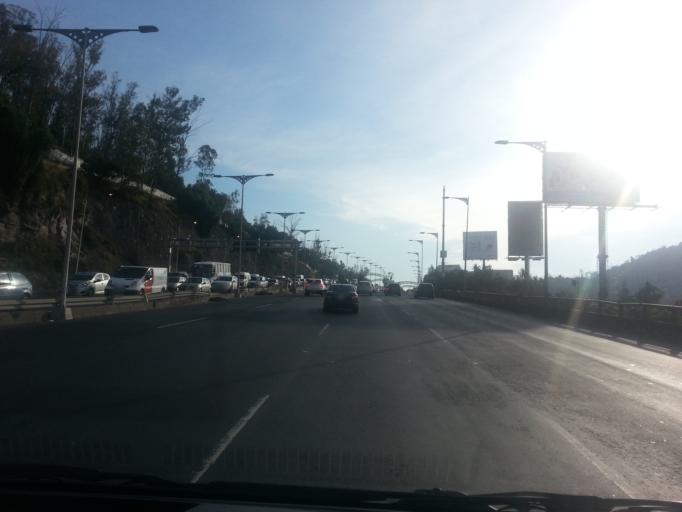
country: MX
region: Mexico City
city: Gustavo A. Madero
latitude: 19.5028
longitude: -99.1157
